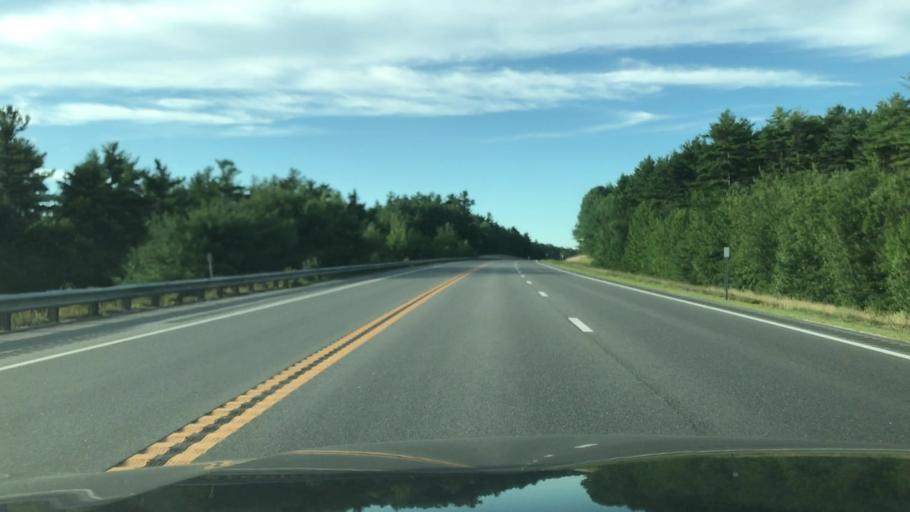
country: US
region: New Hampshire
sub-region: Strafford County
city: Farmington
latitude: 43.4251
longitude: -71.0096
